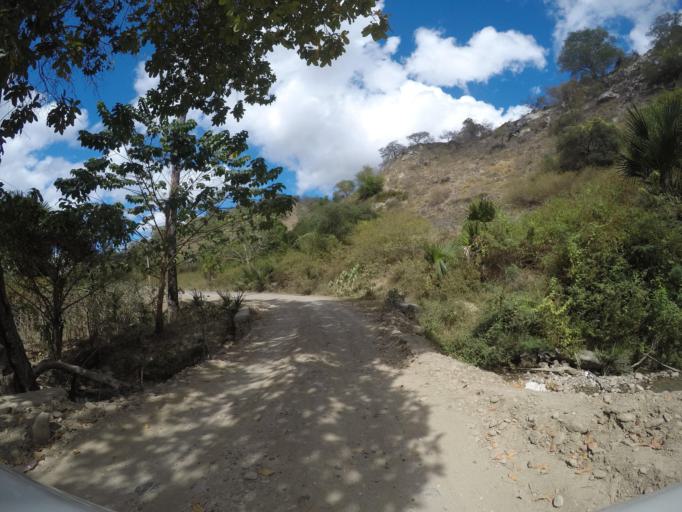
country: TL
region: Lautem
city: Lospalos
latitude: -8.4135
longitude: 126.8266
